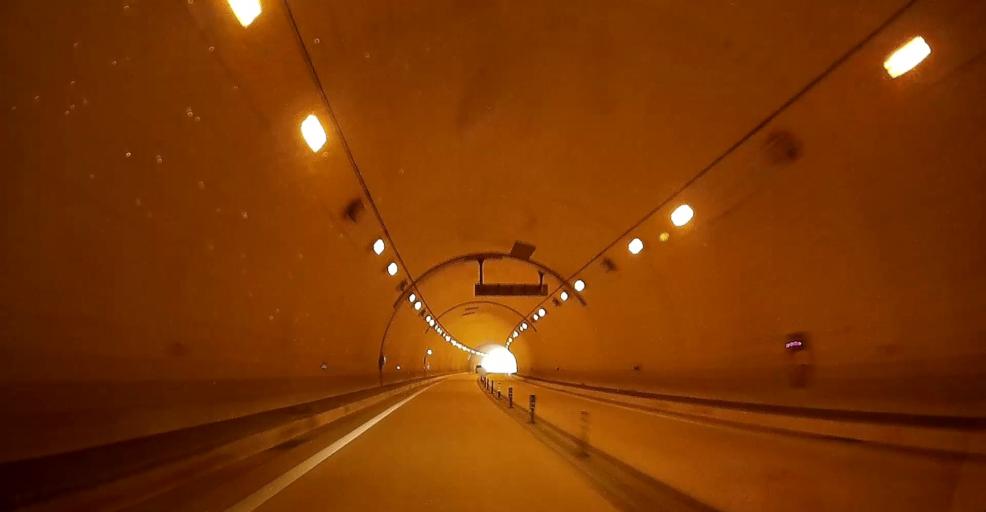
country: JP
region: Kumamoto
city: Yatsushiro
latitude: 32.5056
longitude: 130.4028
